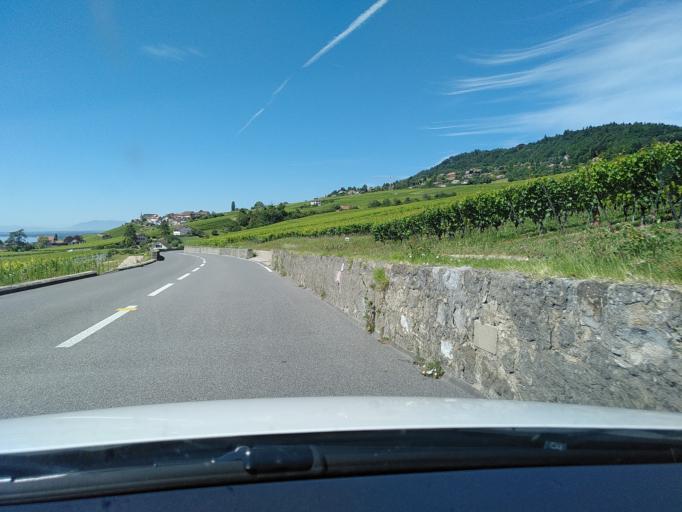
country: CH
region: Vaud
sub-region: Morges District
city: Aubonne
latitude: 46.4865
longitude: 6.3791
